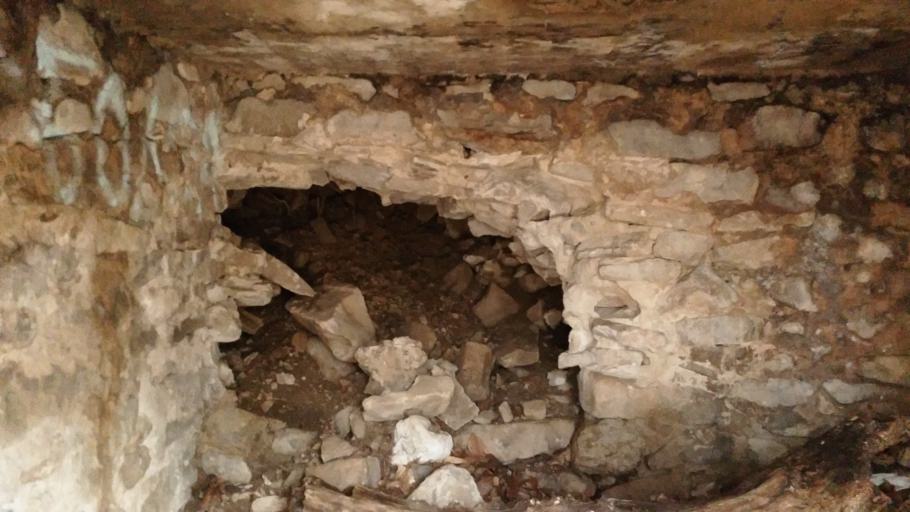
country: RU
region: Stavropol'skiy
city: Zheleznovodsk
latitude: 44.1108
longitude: 43.0263
